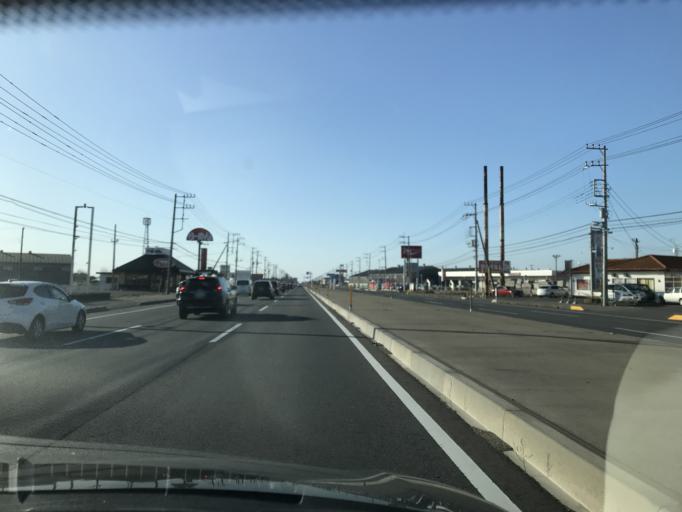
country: JP
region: Chiba
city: Omigawa
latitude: 35.8831
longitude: 140.6790
